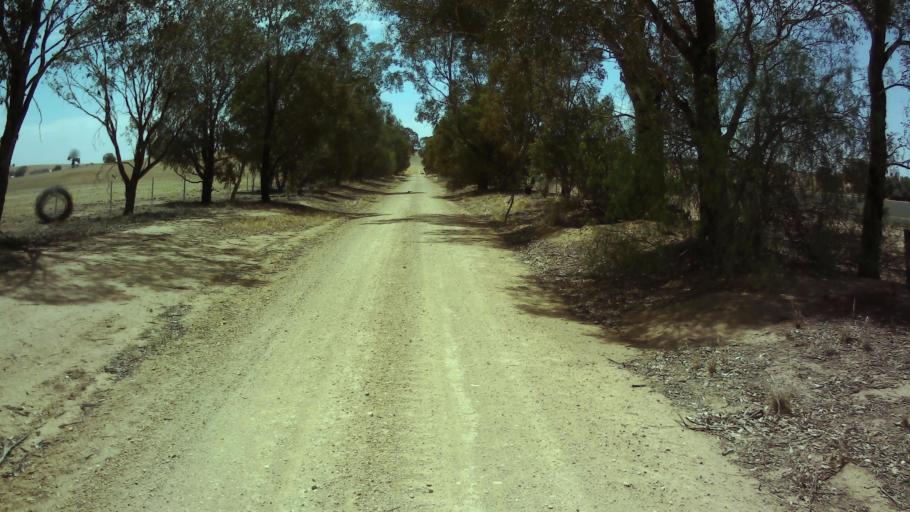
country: AU
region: New South Wales
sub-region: Cowra
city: Cowra
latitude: -33.9581
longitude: 148.4494
